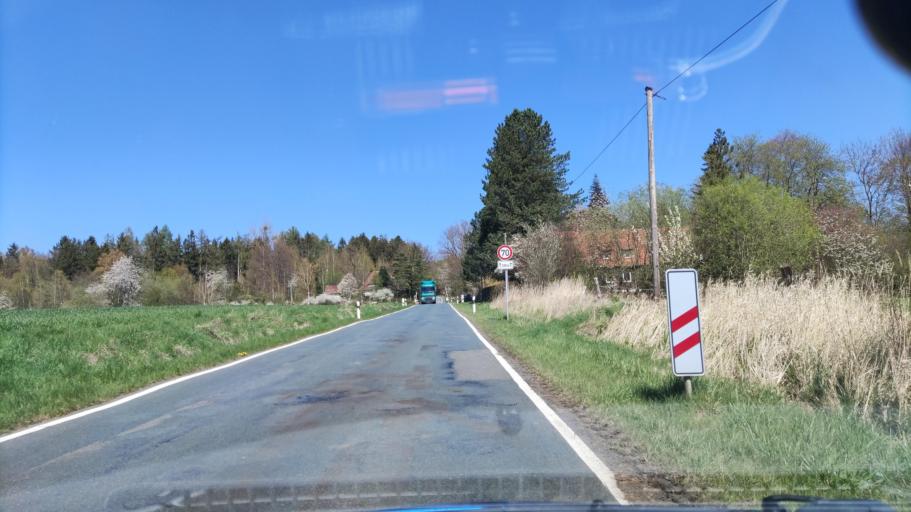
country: DE
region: Lower Saxony
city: Eimen
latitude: 51.8811
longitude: 9.8054
